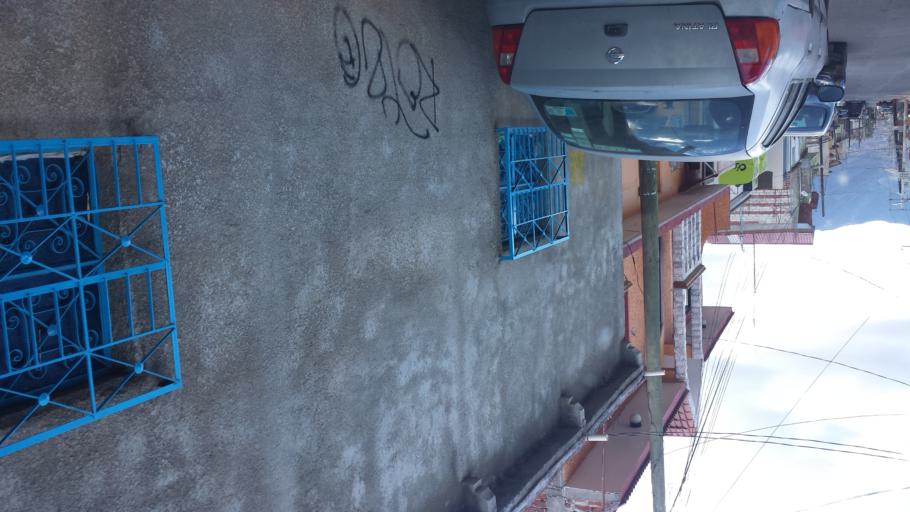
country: MX
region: Oaxaca
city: Tlacolula de Matamoros
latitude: 16.9591
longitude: -96.4792
